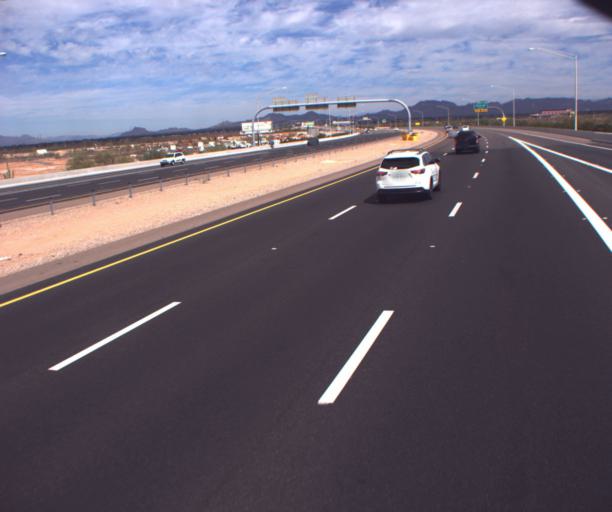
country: US
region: Arizona
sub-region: Maricopa County
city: Queen Creek
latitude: 33.3378
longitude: -111.6449
